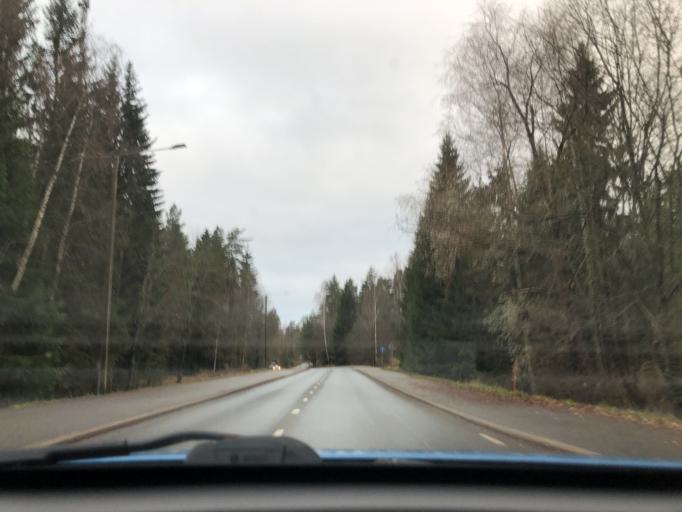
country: FI
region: Pirkanmaa
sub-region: Tampere
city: Kangasala
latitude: 61.5273
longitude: 24.0173
